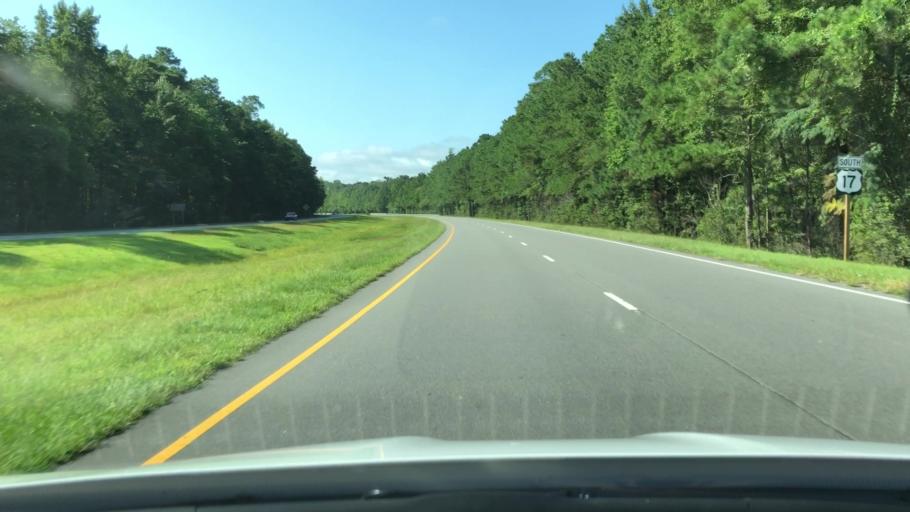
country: US
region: North Carolina
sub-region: Pasquotank County
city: Elizabeth City
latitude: 36.4263
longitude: -76.3425
